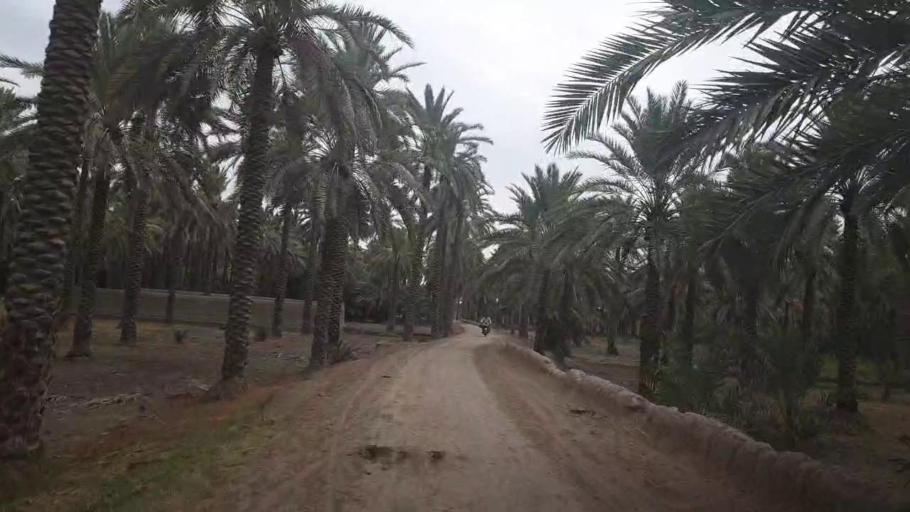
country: PK
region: Sindh
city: Khairpur
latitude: 27.5848
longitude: 68.7491
